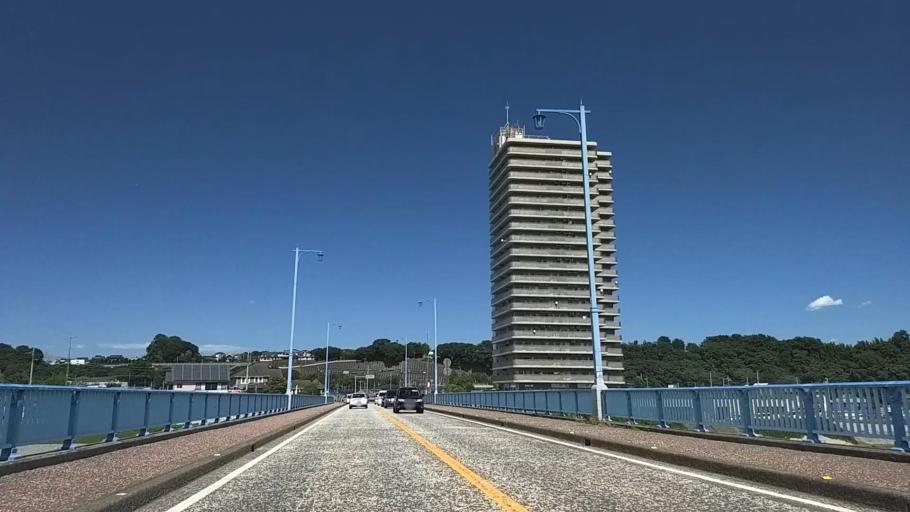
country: JP
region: Kanagawa
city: Zama
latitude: 35.5416
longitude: 139.3304
